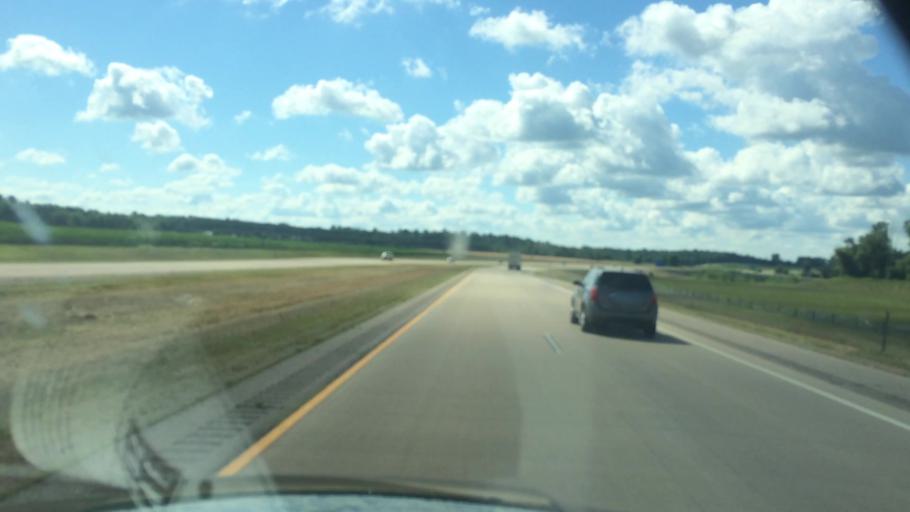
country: US
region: Wisconsin
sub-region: Portage County
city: Amherst
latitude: 44.4646
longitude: -89.3157
